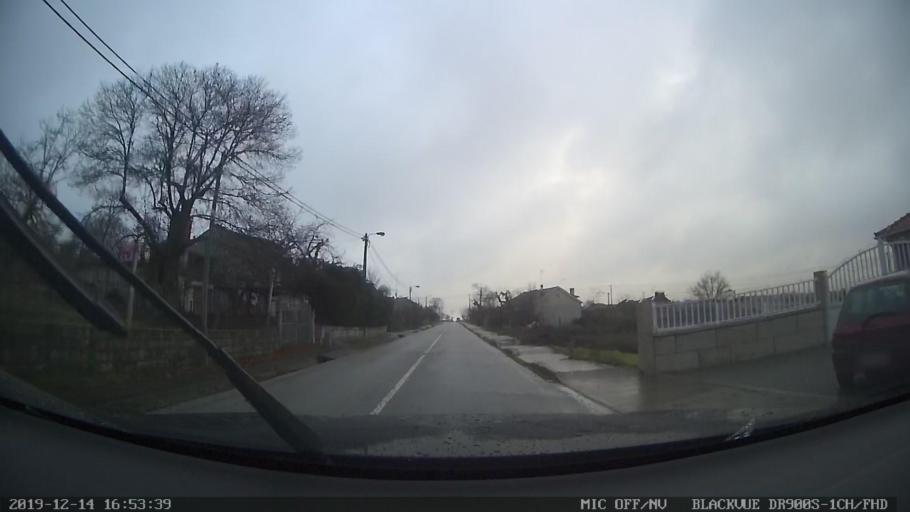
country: PT
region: Vila Real
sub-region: Murca
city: Murca
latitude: 41.4327
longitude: -7.5181
